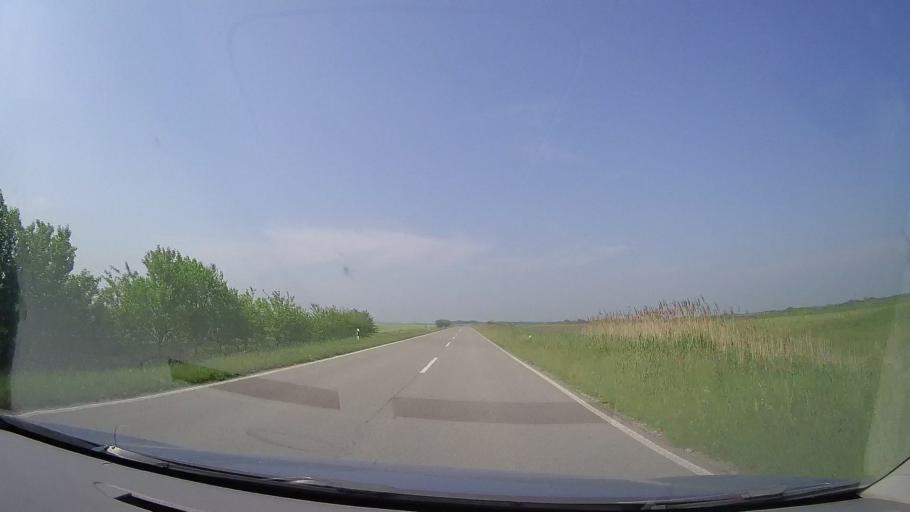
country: RS
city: Boka
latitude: 45.4040
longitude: 20.8183
